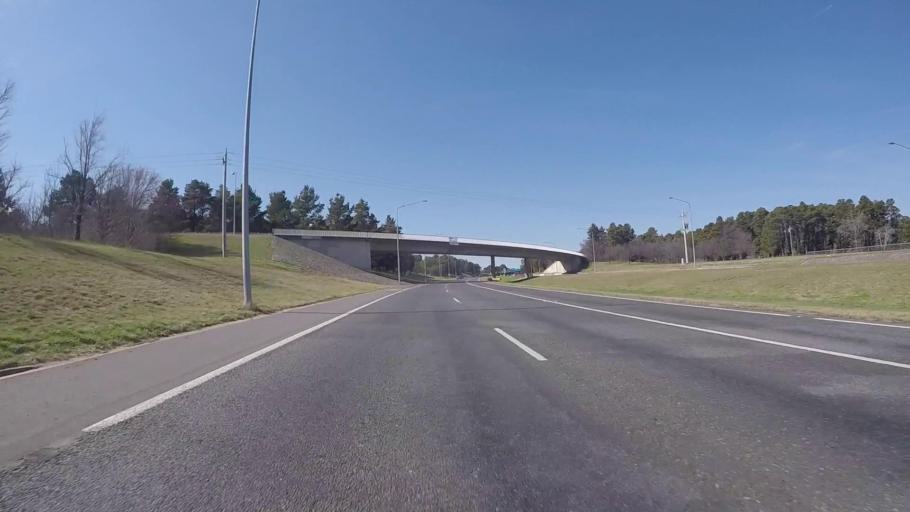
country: AU
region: Australian Capital Territory
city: Forrest
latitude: -35.3153
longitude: 149.0922
